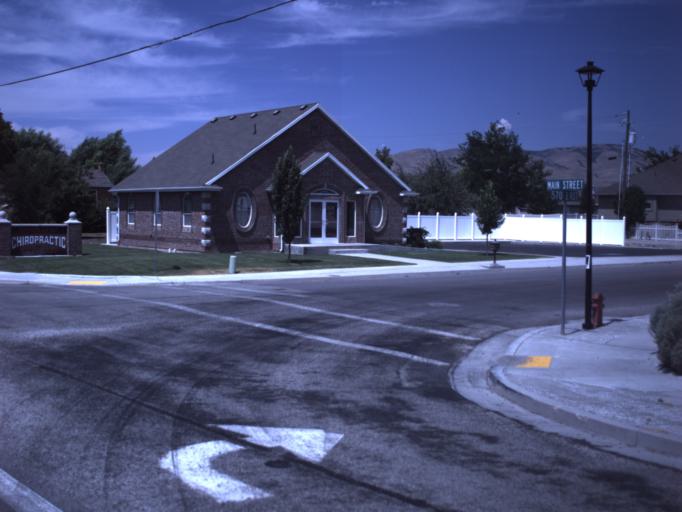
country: US
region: Utah
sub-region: Box Elder County
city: Tremonton
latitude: 41.7120
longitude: -112.1571
